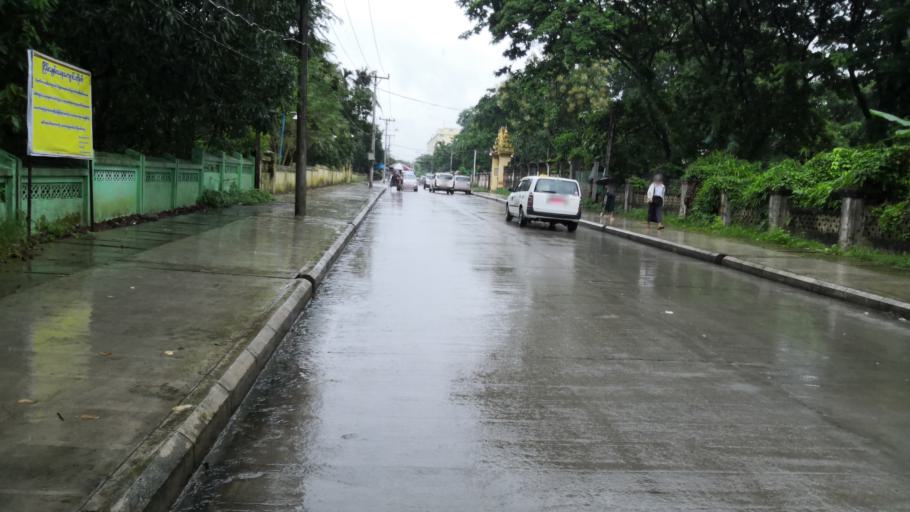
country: MM
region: Yangon
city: Yangon
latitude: 16.8378
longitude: 96.1918
